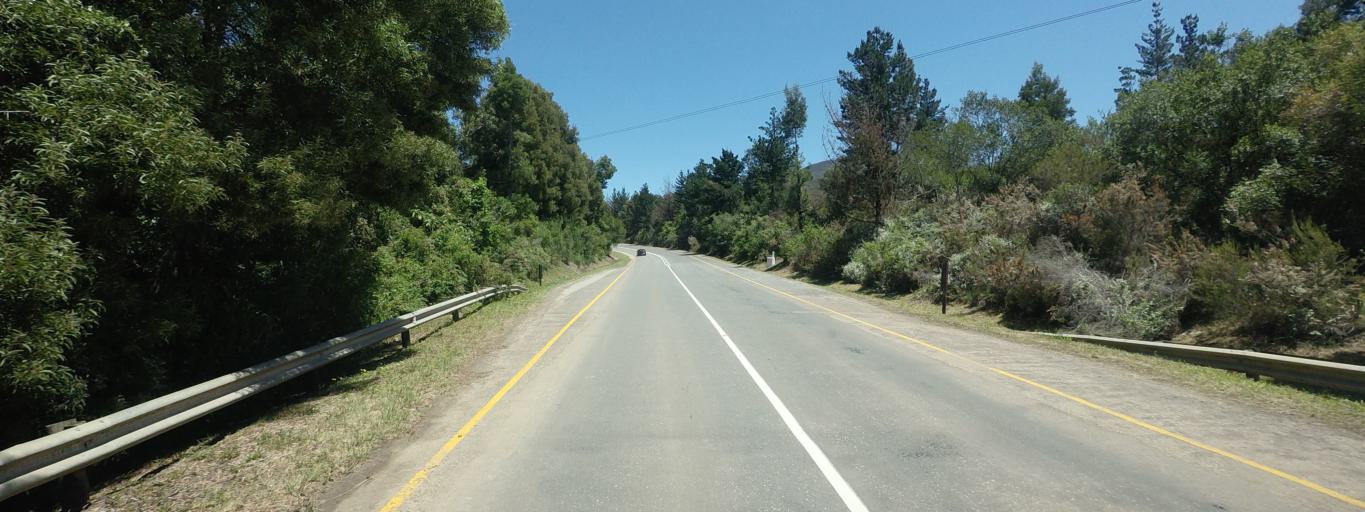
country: ZA
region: Western Cape
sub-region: Eden District Municipality
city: Plettenberg Bay
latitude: -33.9354
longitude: 23.4982
